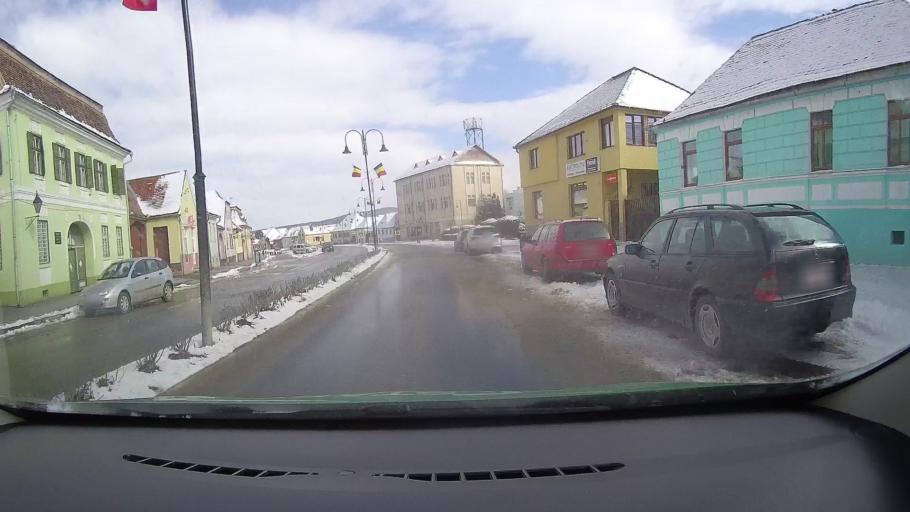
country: RO
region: Sibiu
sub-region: Oras Agnita
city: Agnita
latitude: 45.9754
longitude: 24.6249
